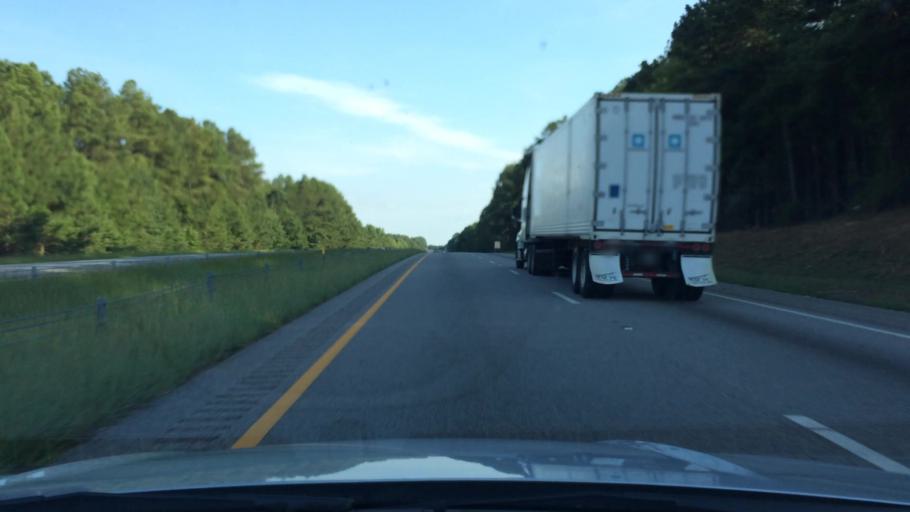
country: US
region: South Carolina
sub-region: Laurens County
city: Clinton
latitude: 34.5762
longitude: -81.8933
